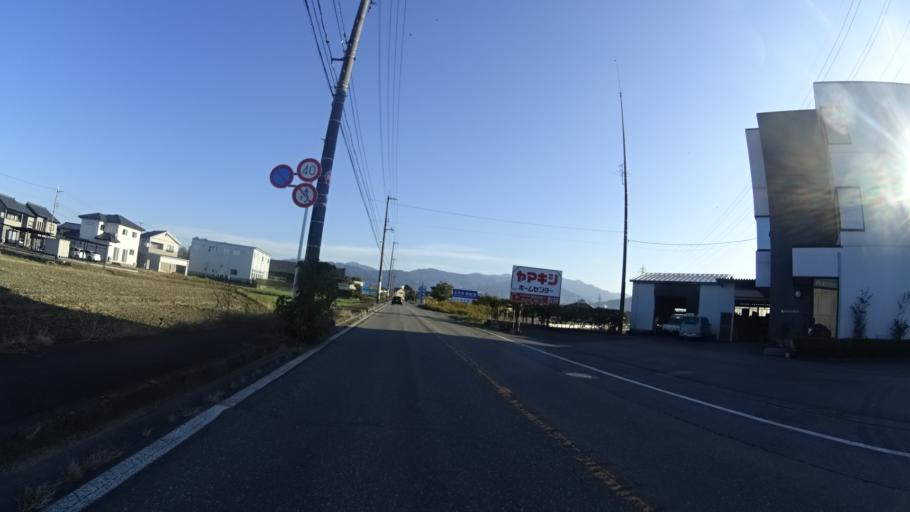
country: JP
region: Fukui
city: Fukui-shi
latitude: 36.0867
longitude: 136.2743
